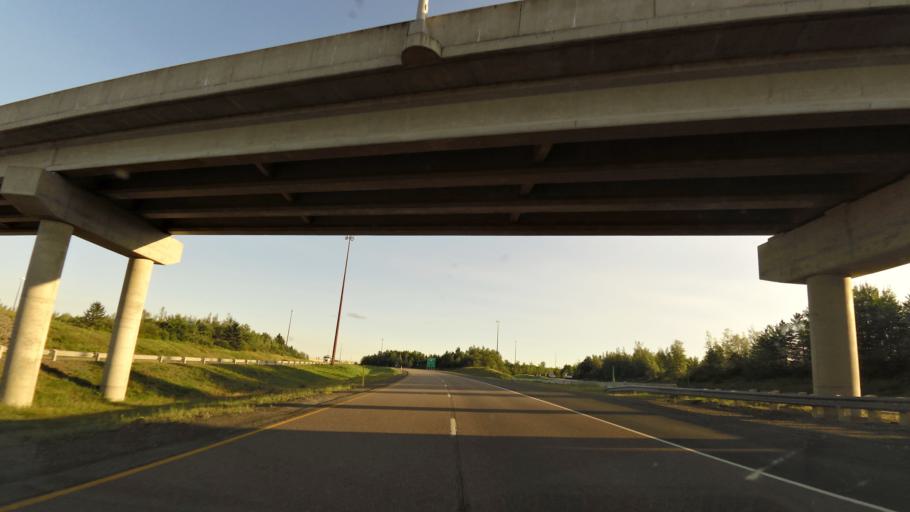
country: CA
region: New Brunswick
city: Salisbury
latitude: 45.9923
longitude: -65.1390
